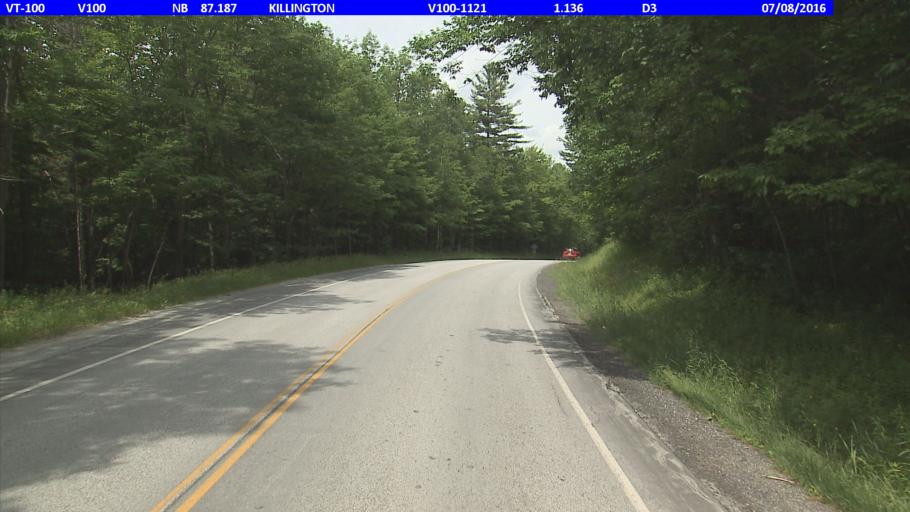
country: US
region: Vermont
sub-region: Rutland County
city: Rutland
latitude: 43.6824
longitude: -72.8132
